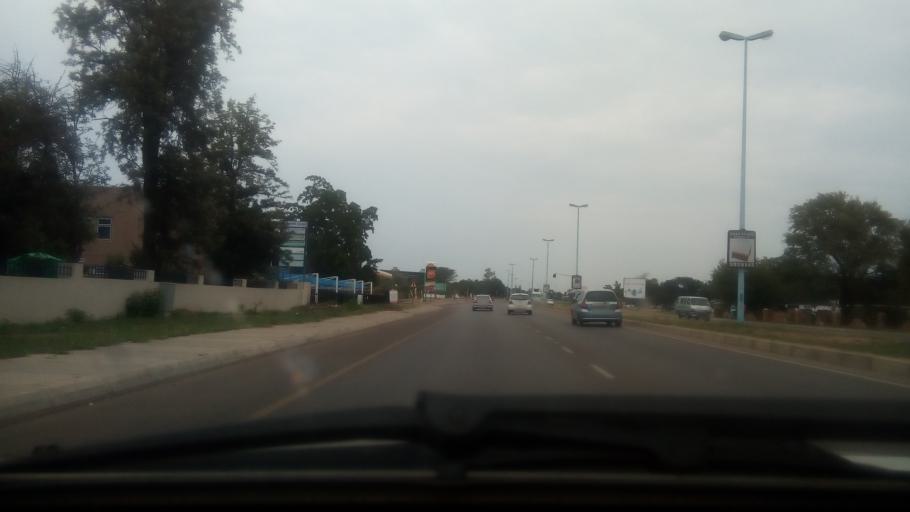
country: BW
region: South East
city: Gaborone
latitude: -24.6763
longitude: 25.9209
